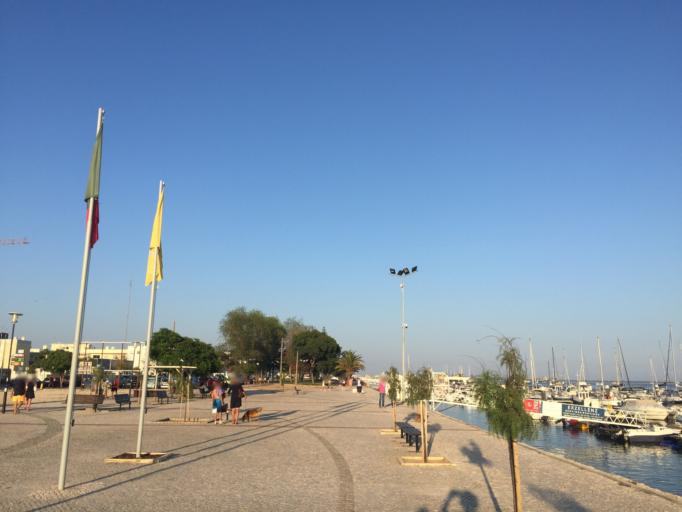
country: PT
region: Faro
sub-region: Olhao
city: Olhao
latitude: 37.0232
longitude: -7.8464
